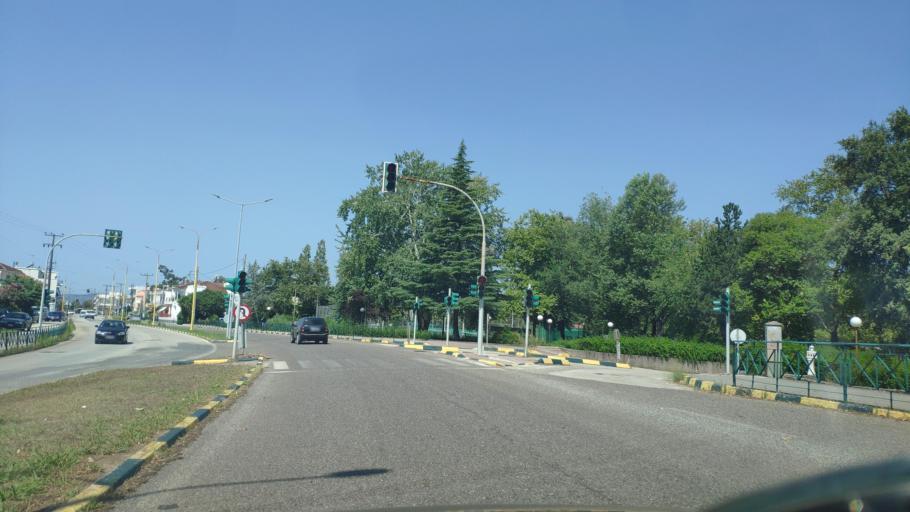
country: GR
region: Epirus
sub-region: Nomos Artas
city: Arta
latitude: 39.1671
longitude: 20.9873
